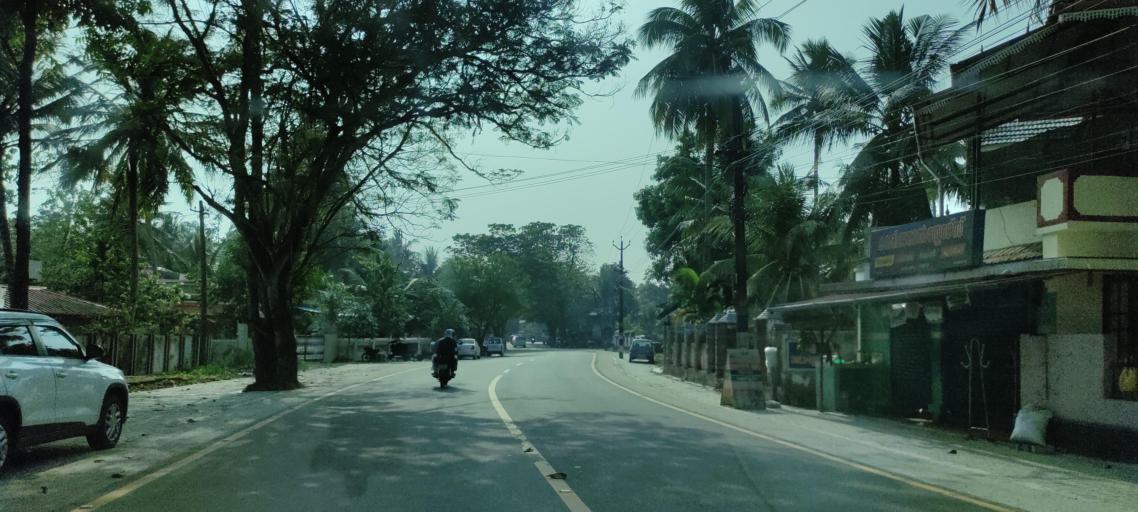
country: IN
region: Kerala
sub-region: Pattanamtitta
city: Tiruvalla
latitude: 9.3689
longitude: 76.5373
